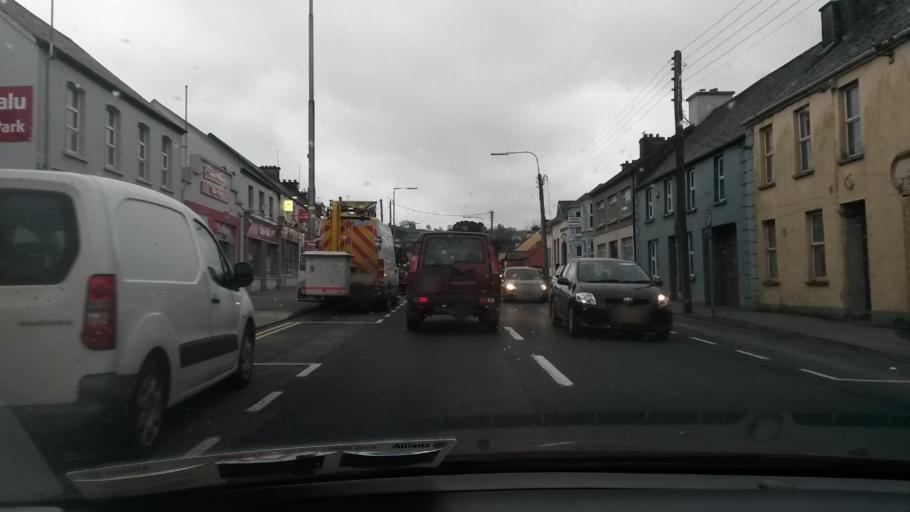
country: IE
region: Munster
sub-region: County Limerick
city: Abbeyfeale
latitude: 52.3832
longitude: -9.3016
